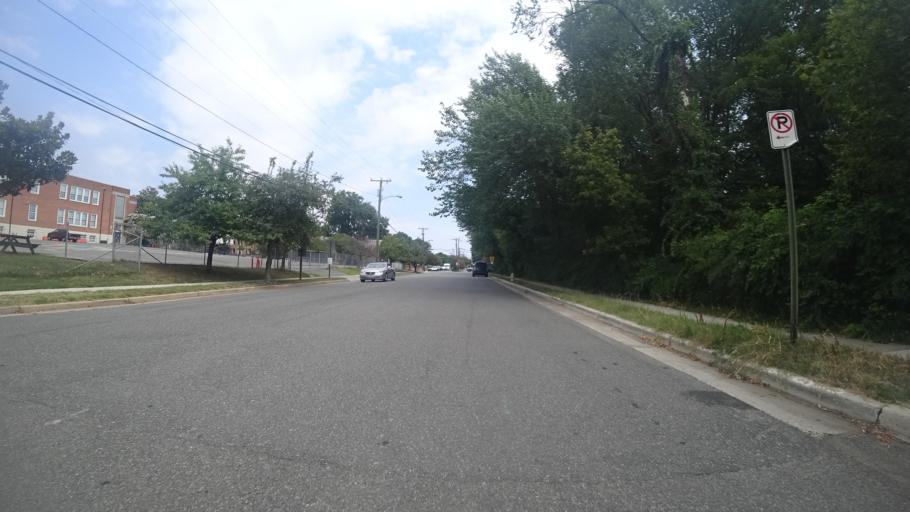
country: US
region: Virginia
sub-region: City of Alexandria
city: Alexandria
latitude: 38.7945
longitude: -77.0457
